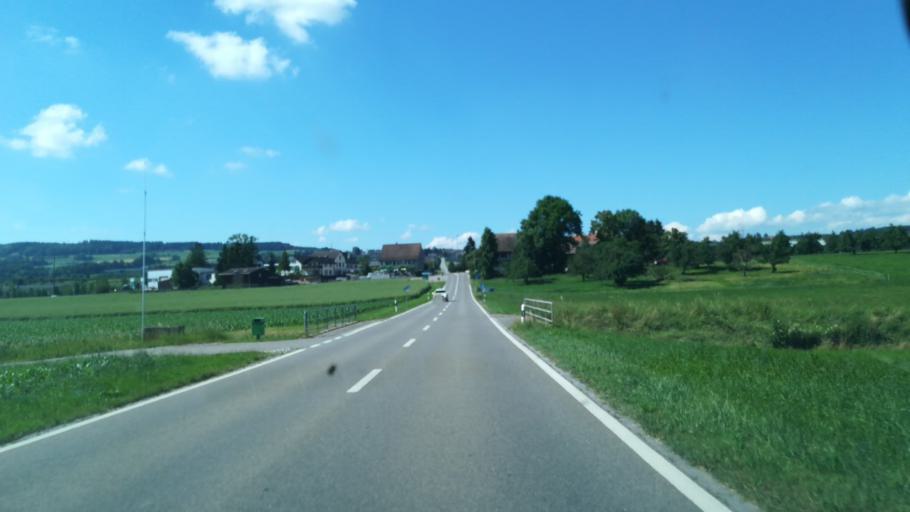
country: CH
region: Thurgau
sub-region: Weinfelden District
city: Sulgen
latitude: 47.5573
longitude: 9.1749
